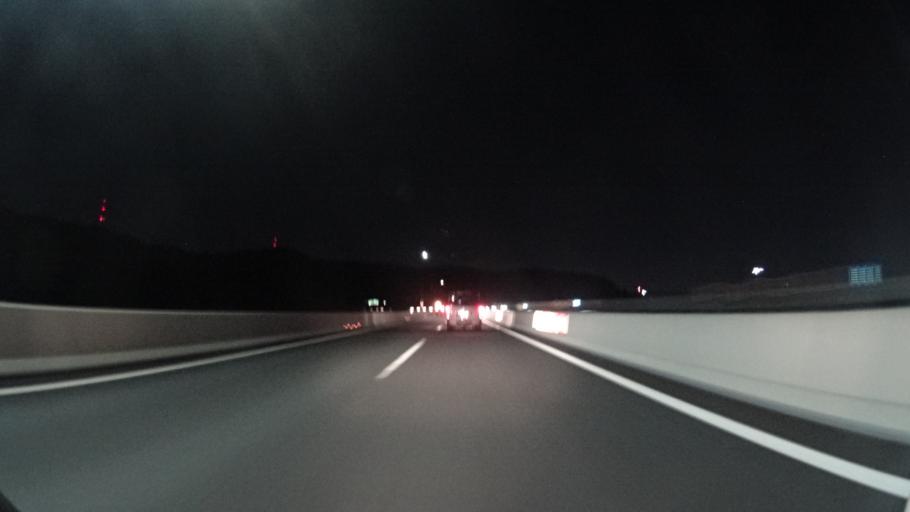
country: JP
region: Osaka
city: Takatsuki
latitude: 34.8859
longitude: 135.6175
